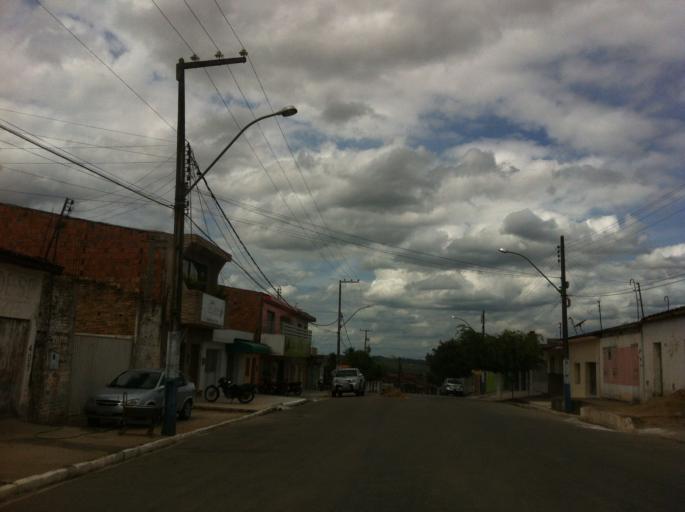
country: BR
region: Alagoas
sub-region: Ibateguara
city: Ibateguara
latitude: -8.9692
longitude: -35.9254
